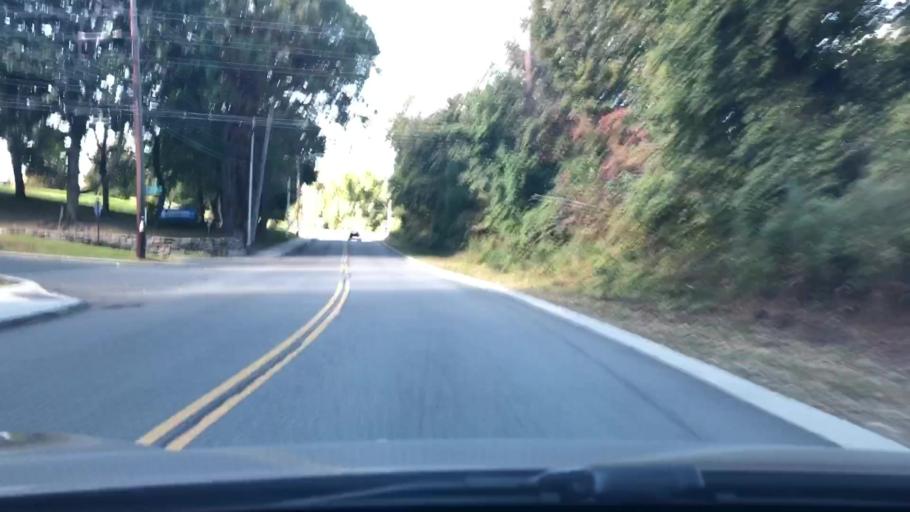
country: US
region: New York
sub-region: Westchester County
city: Rye
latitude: 40.9751
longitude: -73.6974
